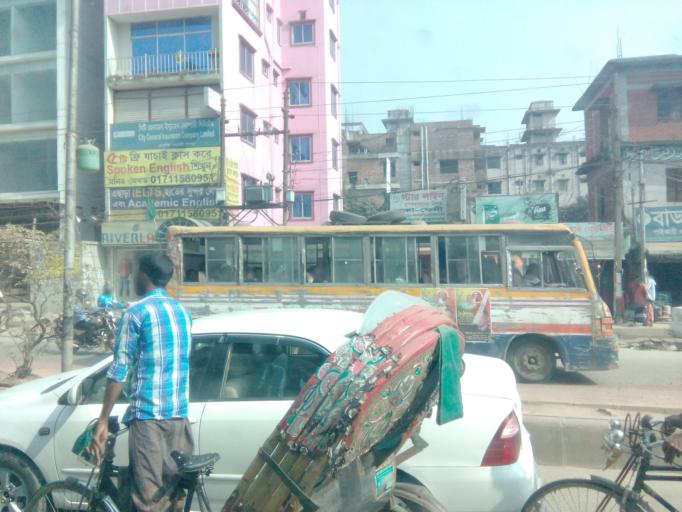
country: BD
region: Dhaka
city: Paltan
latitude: 23.7790
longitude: 90.4257
